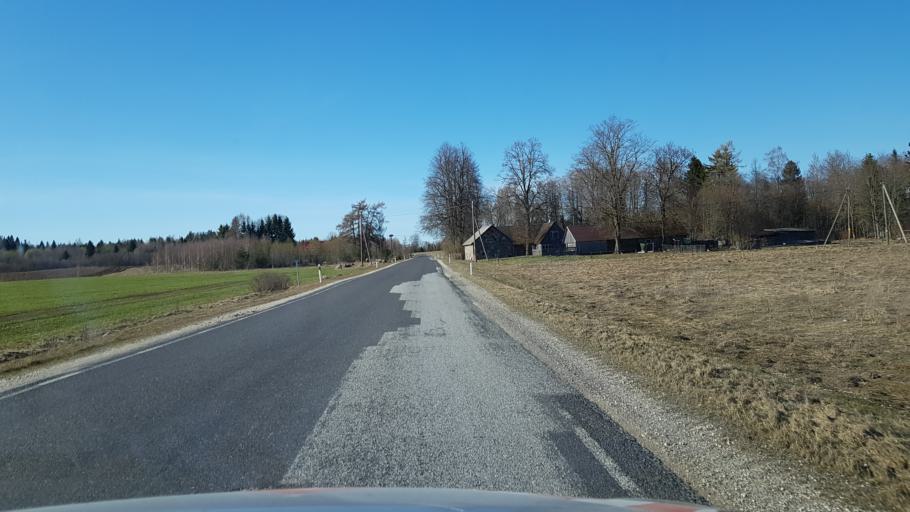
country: EE
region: Laeaene-Virumaa
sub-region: Vinni vald
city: Vinni
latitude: 59.3031
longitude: 26.5338
